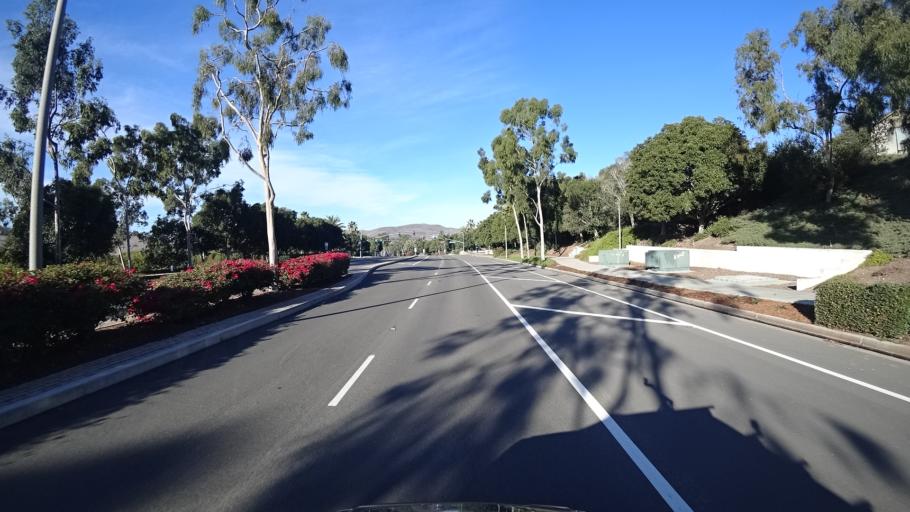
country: US
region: California
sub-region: Orange County
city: San Clemente
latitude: 33.4586
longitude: -117.5857
